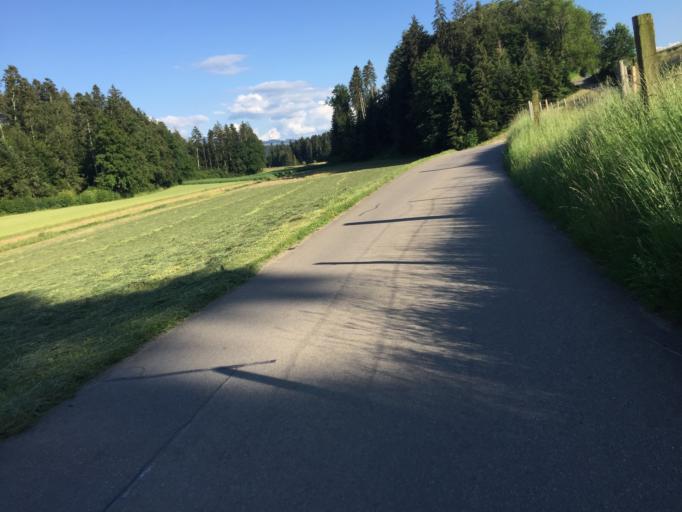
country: CH
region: Bern
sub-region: Bern-Mittelland District
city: Niederwichtrach
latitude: 46.8385
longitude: 7.5824
